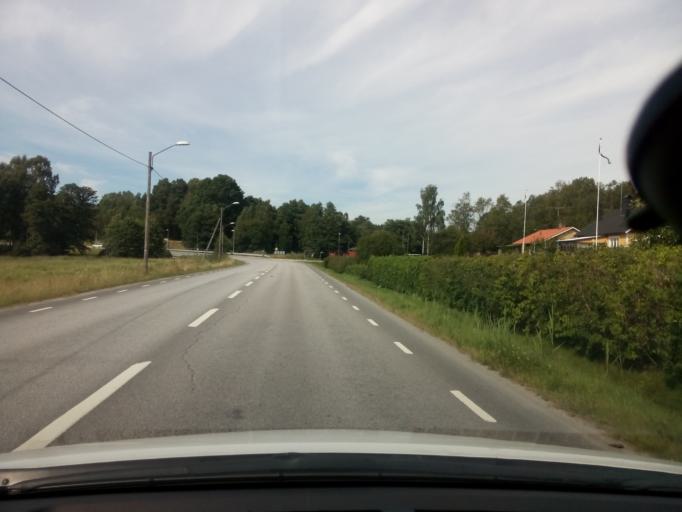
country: SE
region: Soedermanland
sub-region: Nykopings Kommun
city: Nykoping
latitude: 58.7753
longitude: 17.0841
